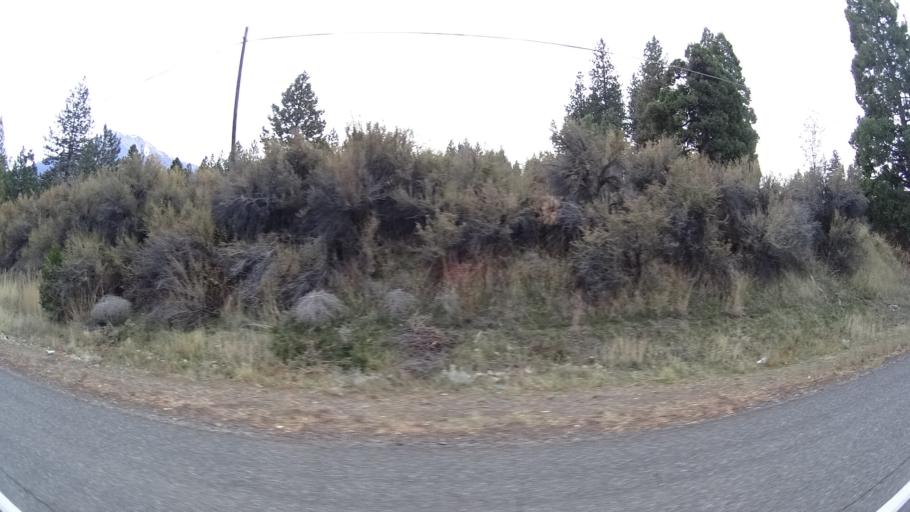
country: US
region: California
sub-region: Siskiyou County
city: Weed
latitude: 41.4450
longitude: -122.3699
